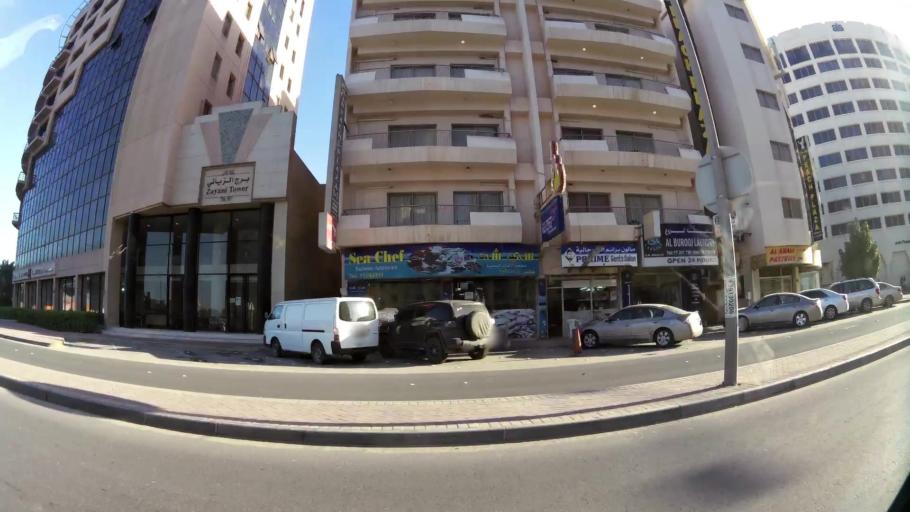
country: BH
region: Manama
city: Manama
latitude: 26.2343
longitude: 50.5971
